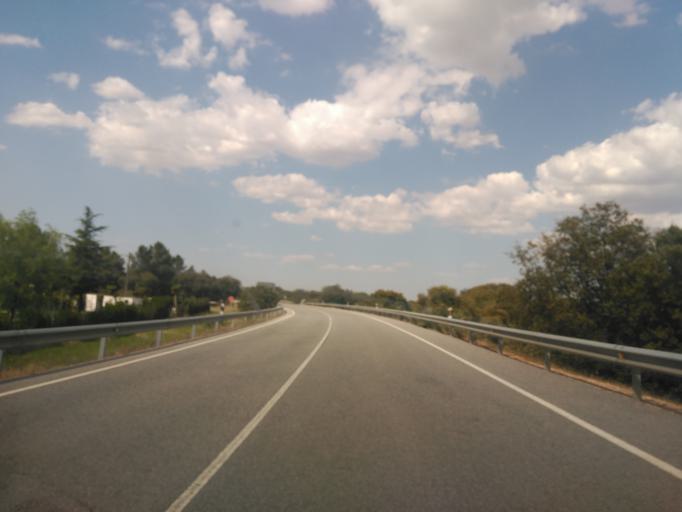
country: ES
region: Castille and Leon
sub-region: Provincia de Salamanca
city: Martinamor
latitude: 40.8119
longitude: -5.6292
